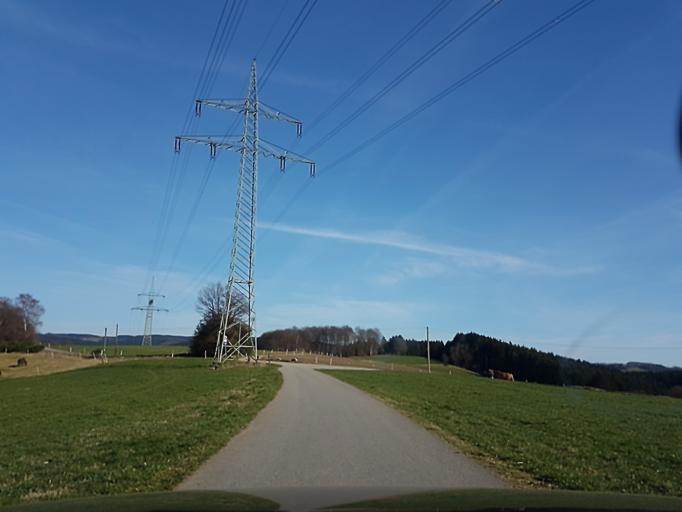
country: DE
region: North Rhine-Westphalia
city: Kierspe
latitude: 51.1415
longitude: 7.6048
